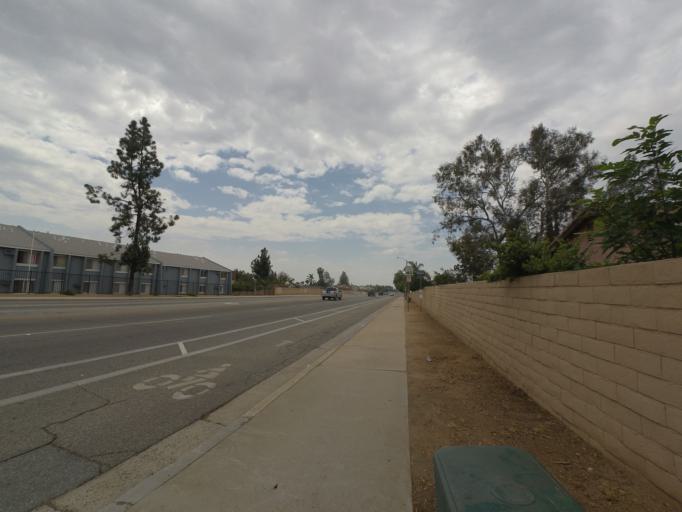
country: US
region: California
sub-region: Riverside County
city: Moreno Valley
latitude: 33.9281
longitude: -117.2439
